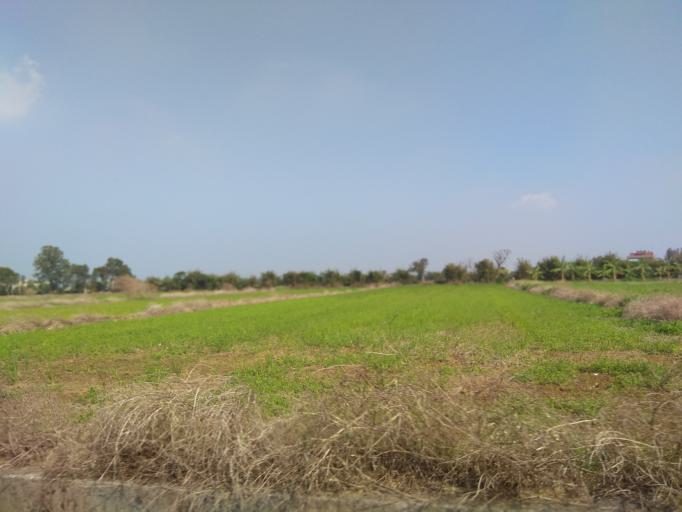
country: TW
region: Taiwan
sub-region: Hsinchu
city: Zhubei
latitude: 24.9968
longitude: 121.0620
